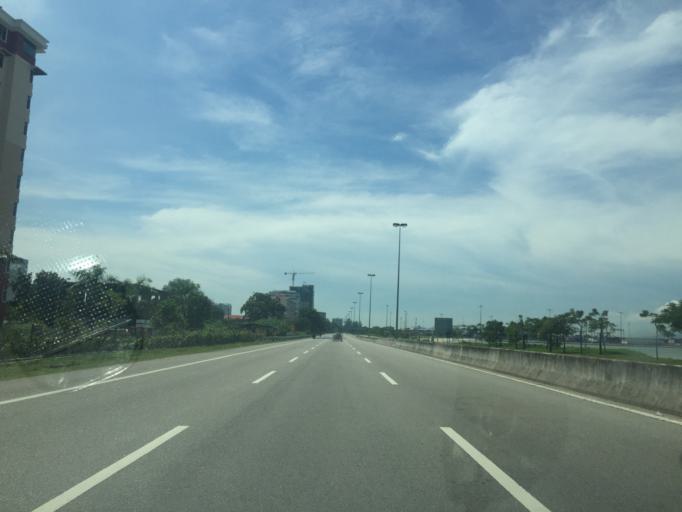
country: MY
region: Penang
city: Butterworth
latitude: 5.4255
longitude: 100.3752
